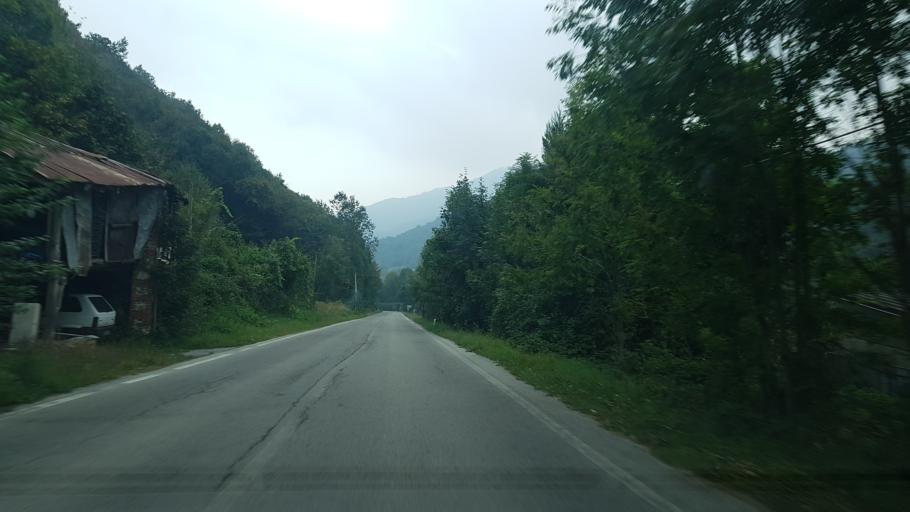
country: IT
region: Piedmont
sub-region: Provincia di Cuneo
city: Roccaforte Mondovi
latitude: 44.2876
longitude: 7.7450
